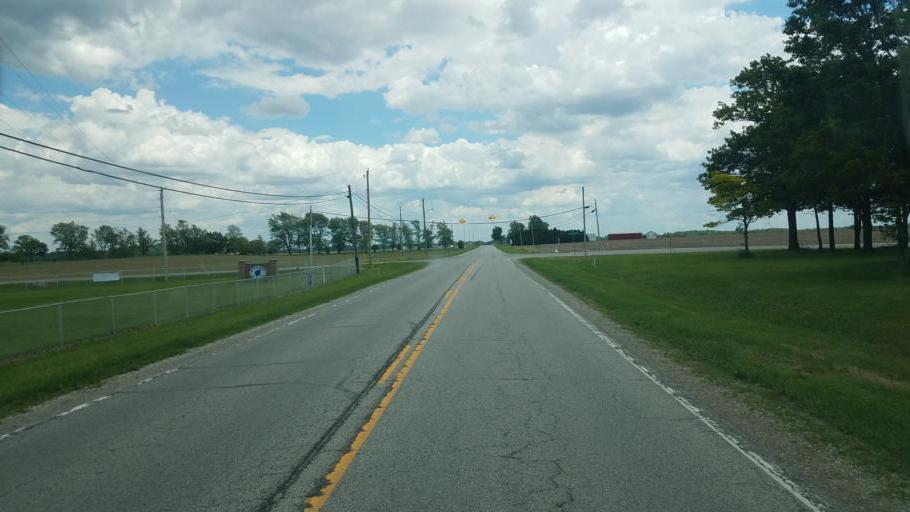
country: US
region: Ohio
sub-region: Crawford County
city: Bucyrus
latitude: 40.8195
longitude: -83.0177
